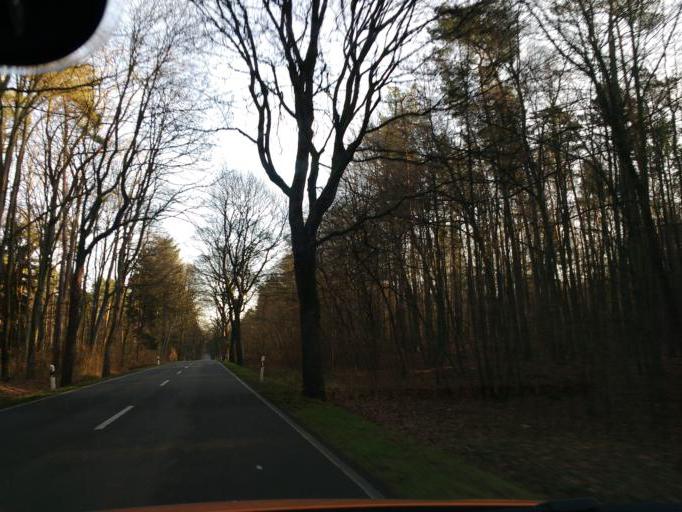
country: DE
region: Brandenburg
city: Protzel
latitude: 52.6464
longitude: 13.9276
